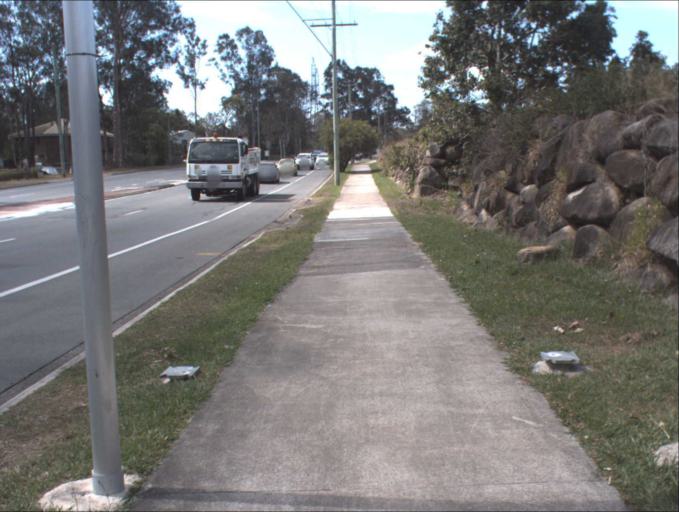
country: AU
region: Queensland
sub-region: Logan
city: Slacks Creek
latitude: -27.6614
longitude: 153.1408
